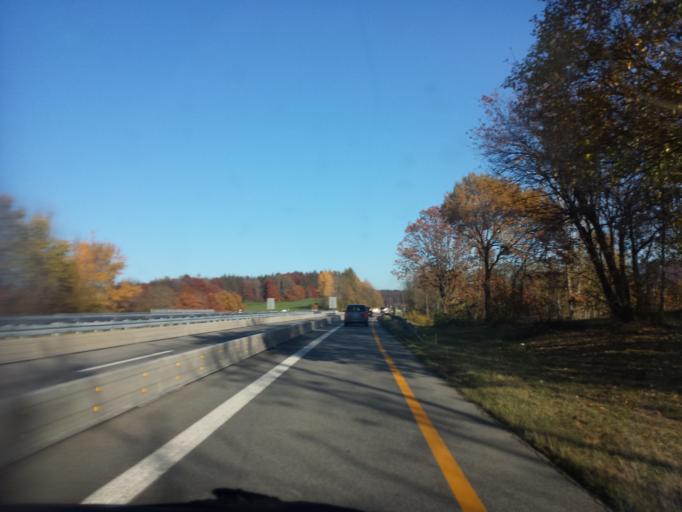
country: DE
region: Bavaria
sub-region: Upper Bavaria
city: Ohlstadt
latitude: 47.6627
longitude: 11.2478
